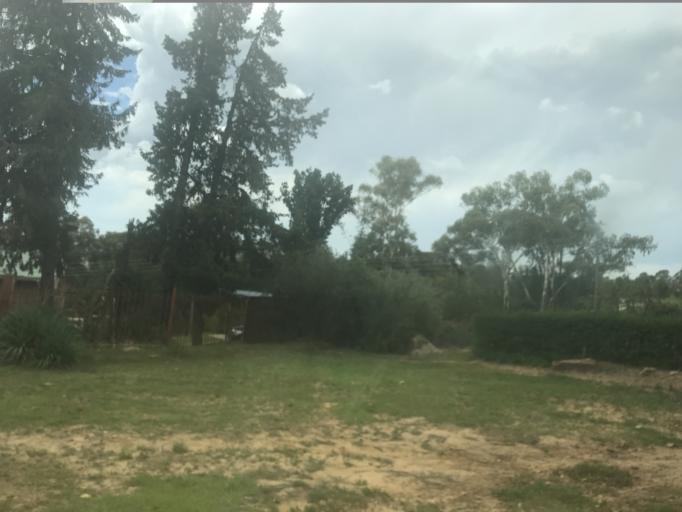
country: LS
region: Maseru
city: Nako
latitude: -29.6317
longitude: 27.5096
